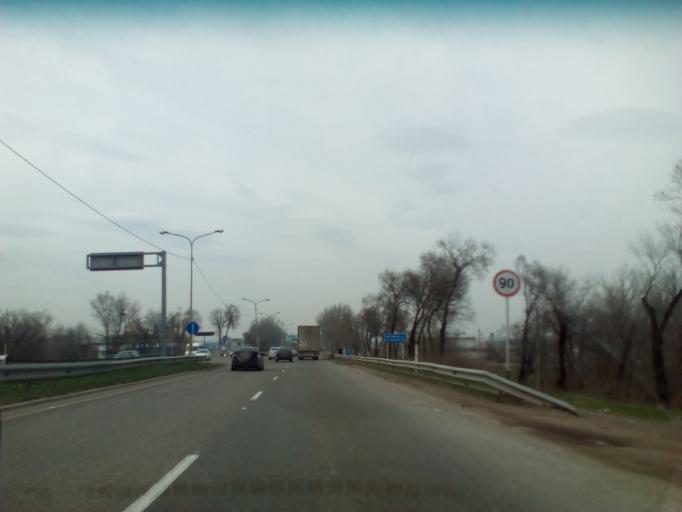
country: KZ
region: Almaty Oblysy
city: Burunday
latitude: 43.2191
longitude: 76.6417
